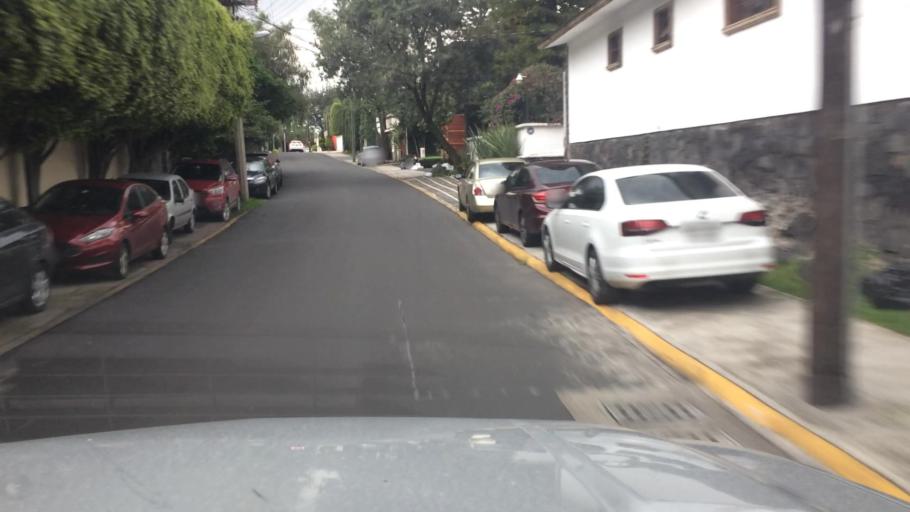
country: MX
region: Mexico City
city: Magdalena Contreras
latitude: 19.3232
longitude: -99.2074
